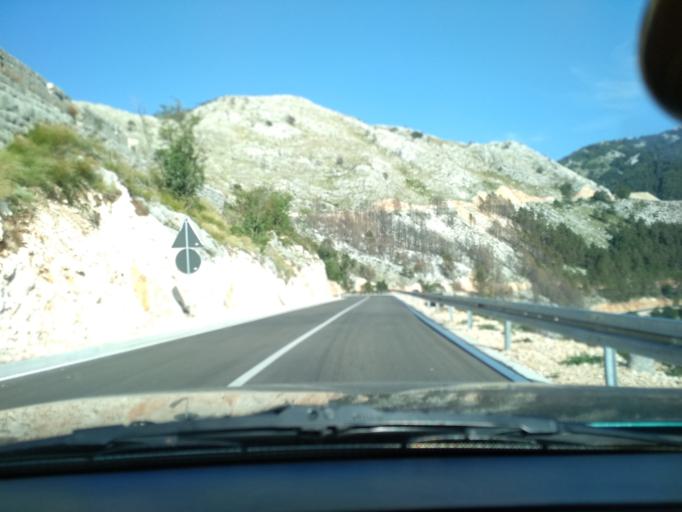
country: ME
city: Dobrota
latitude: 42.4387
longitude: 18.8367
